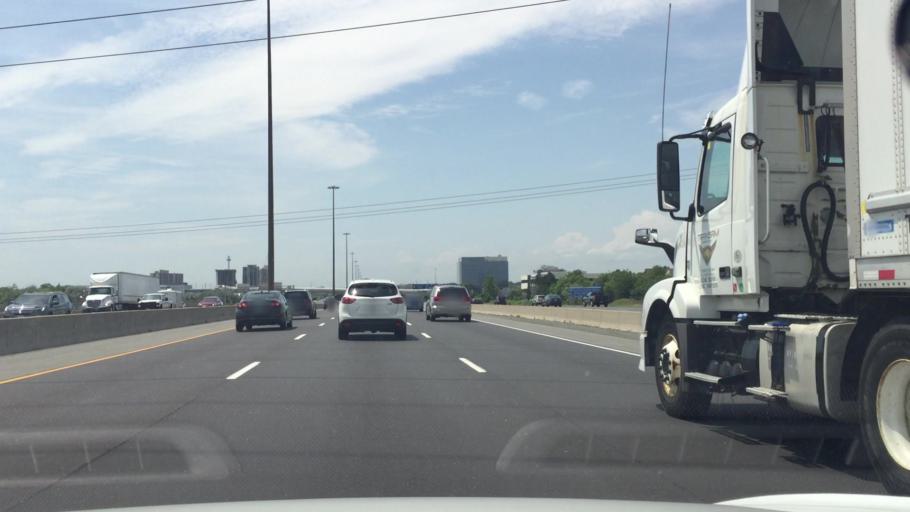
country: CA
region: Ontario
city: Ajax
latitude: 43.8370
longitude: -79.0766
